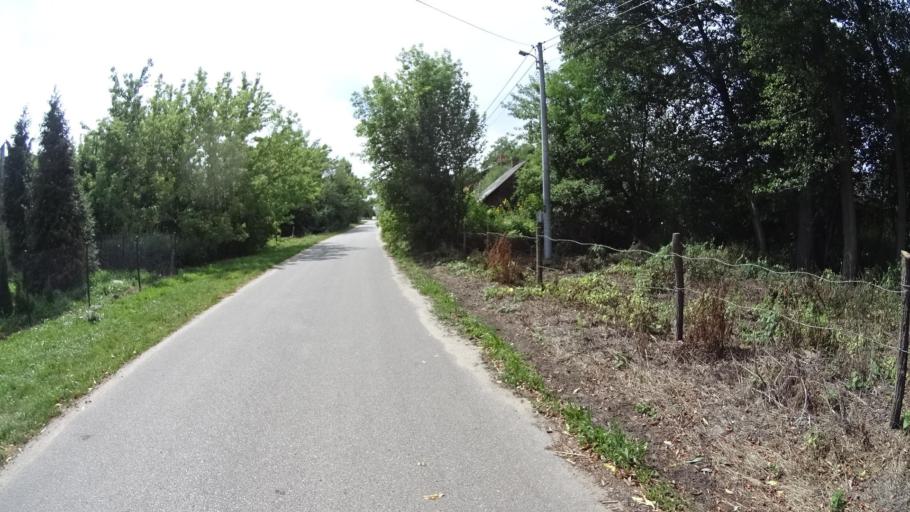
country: PL
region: Masovian Voivodeship
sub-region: Powiat bialobrzeski
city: Wysmierzyce
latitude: 51.6355
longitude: 20.8590
